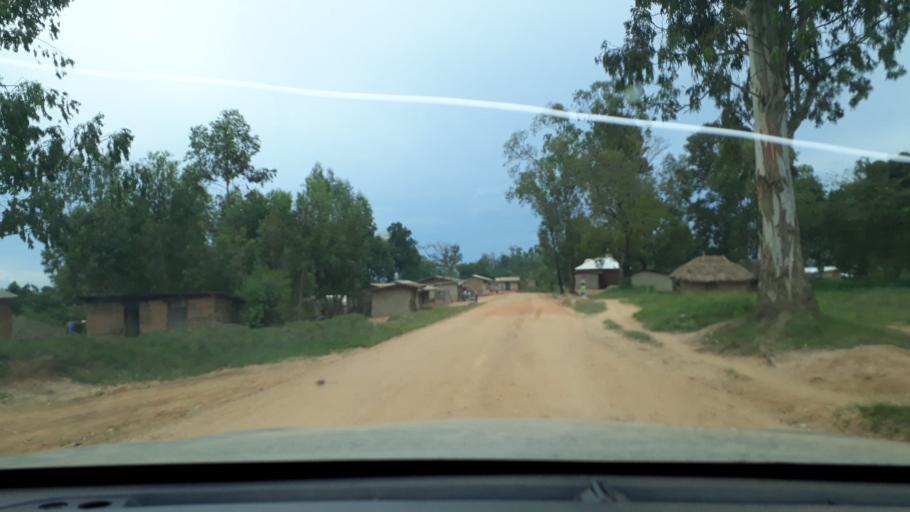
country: CD
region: Eastern Province
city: Bunia
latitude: 1.8529
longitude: 30.4787
